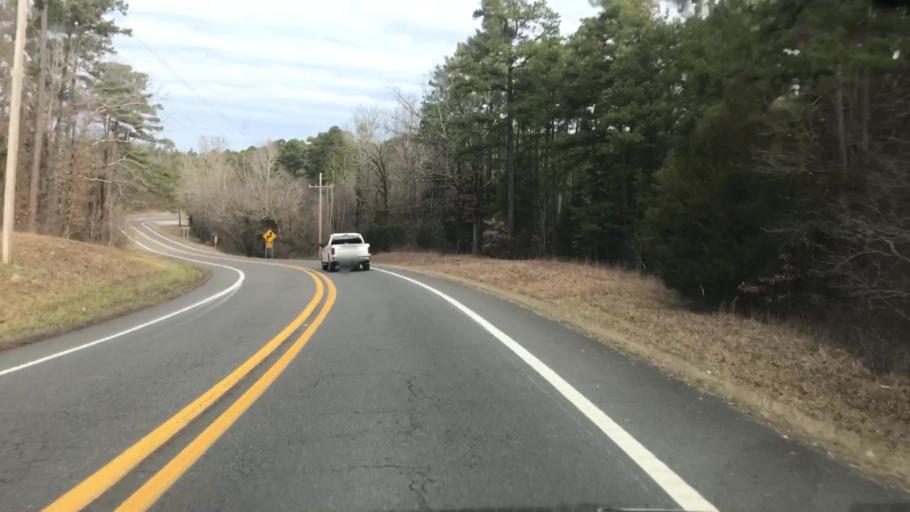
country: US
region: Arkansas
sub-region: Montgomery County
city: Mount Ida
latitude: 34.5906
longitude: -93.6644
